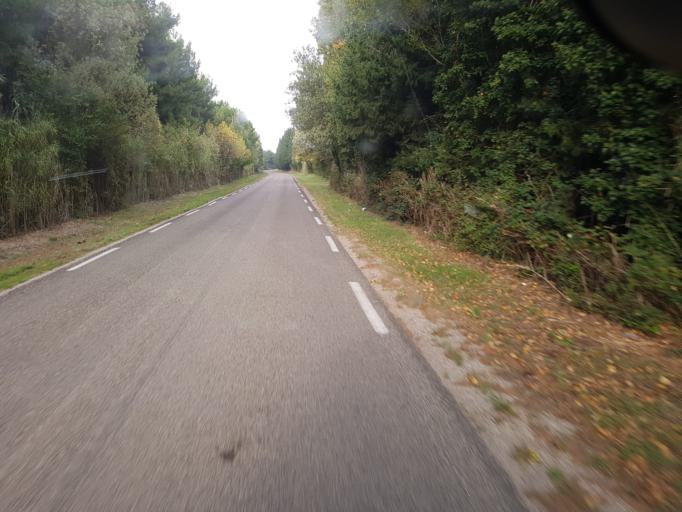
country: FR
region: Languedoc-Roussillon
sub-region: Departement du Gard
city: Aramon
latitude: 43.8867
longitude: 4.6963
